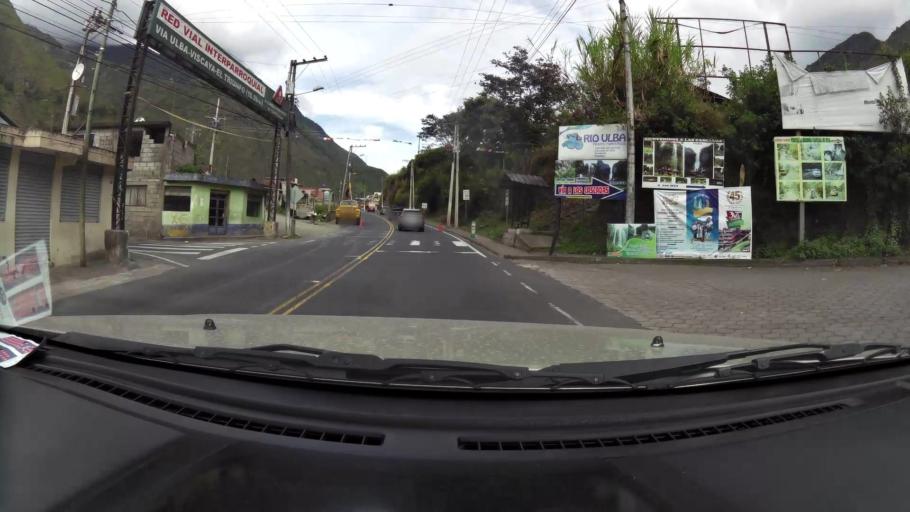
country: EC
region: Tungurahua
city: Banos
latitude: -1.3947
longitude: -78.3984
